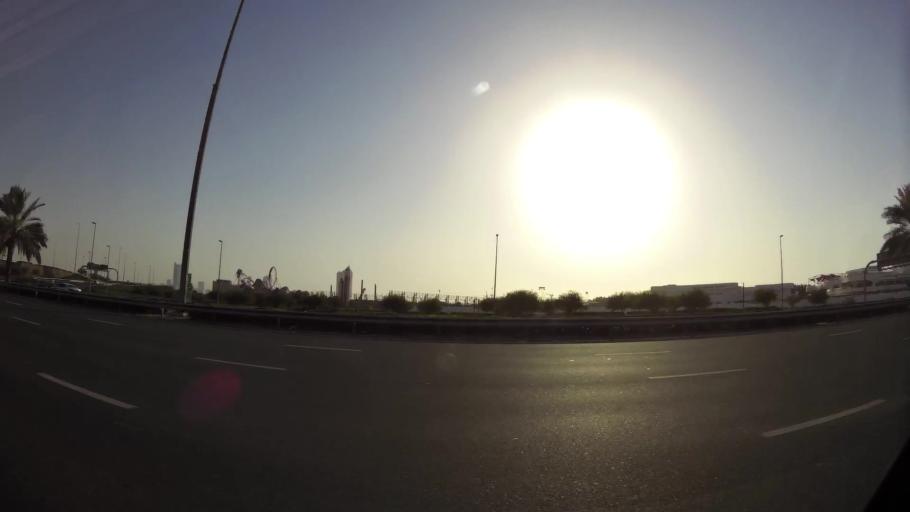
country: AE
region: Dubai
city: Dubai
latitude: 25.0606
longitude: 55.2497
